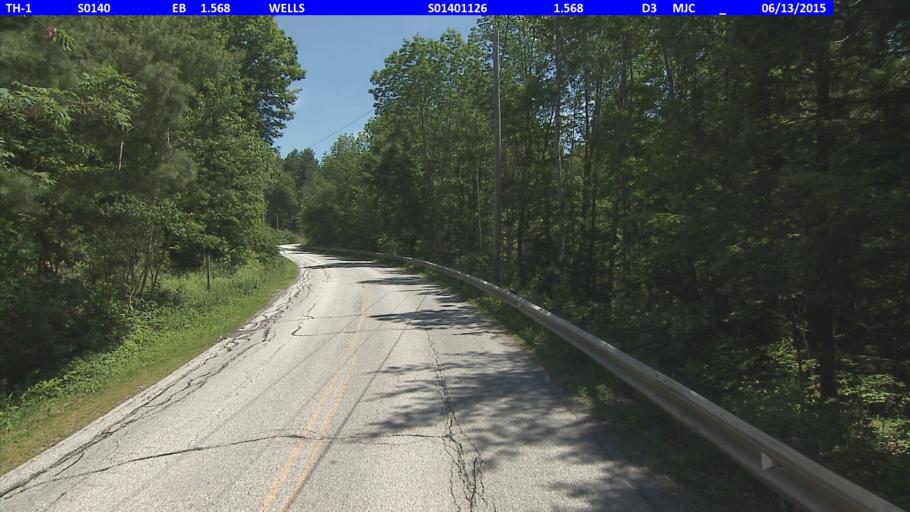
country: US
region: New York
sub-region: Washington County
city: Granville
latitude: 43.4133
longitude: -73.1747
